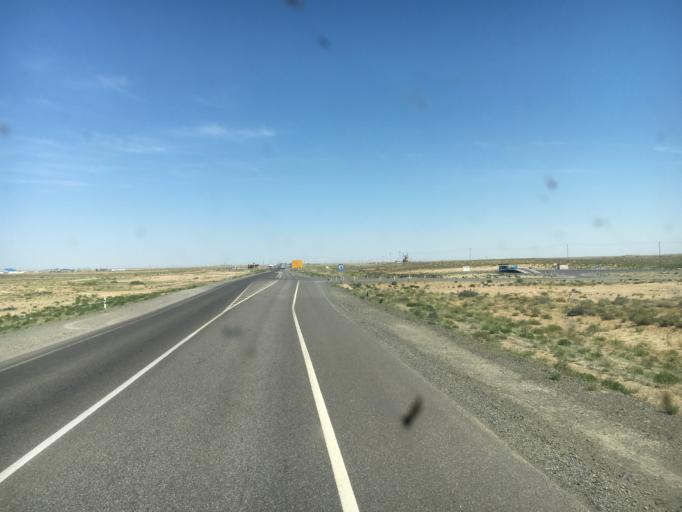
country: KZ
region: Qyzylorda
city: Aral
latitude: 46.7925
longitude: 61.7148
